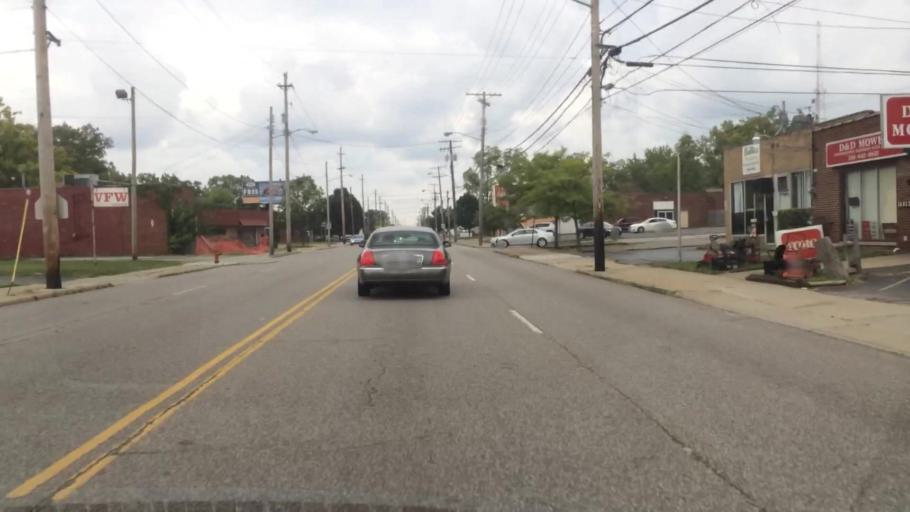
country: US
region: Ohio
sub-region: Cuyahoga County
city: Maple Heights
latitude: 41.4121
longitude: -81.5655
